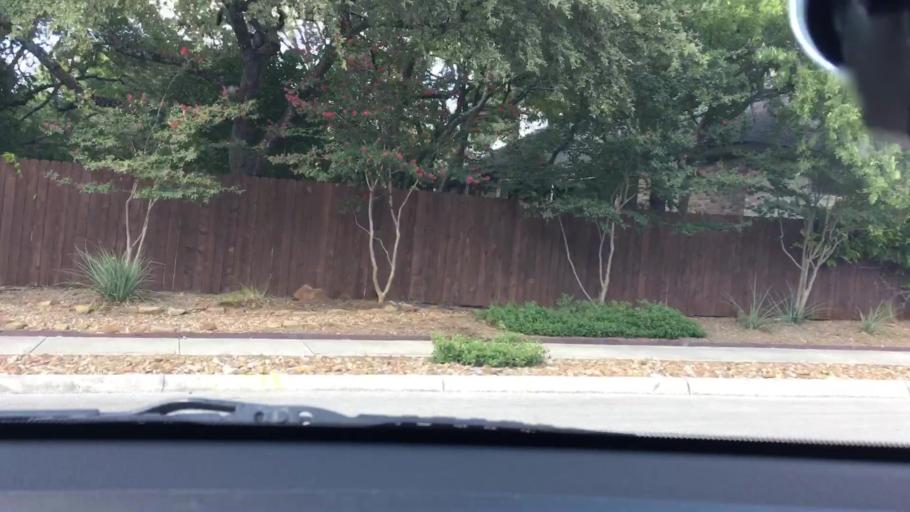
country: US
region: Texas
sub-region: Bexar County
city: Selma
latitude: 29.5721
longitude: -98.3139
